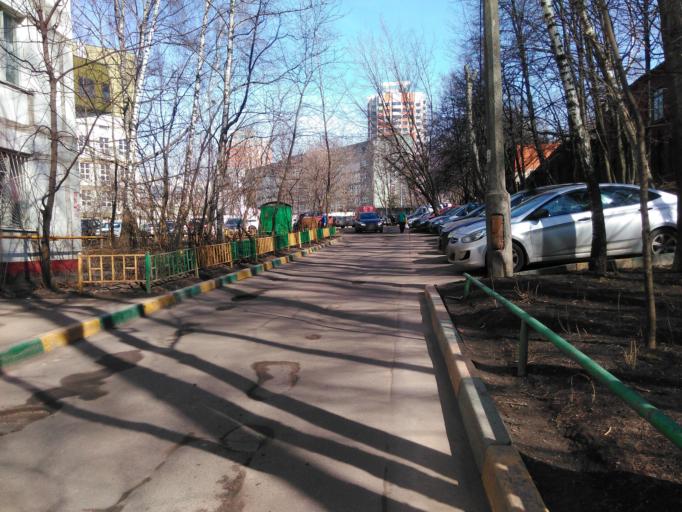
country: RU
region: Moscow
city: Troparevo
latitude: 55.6686
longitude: 37.5030
